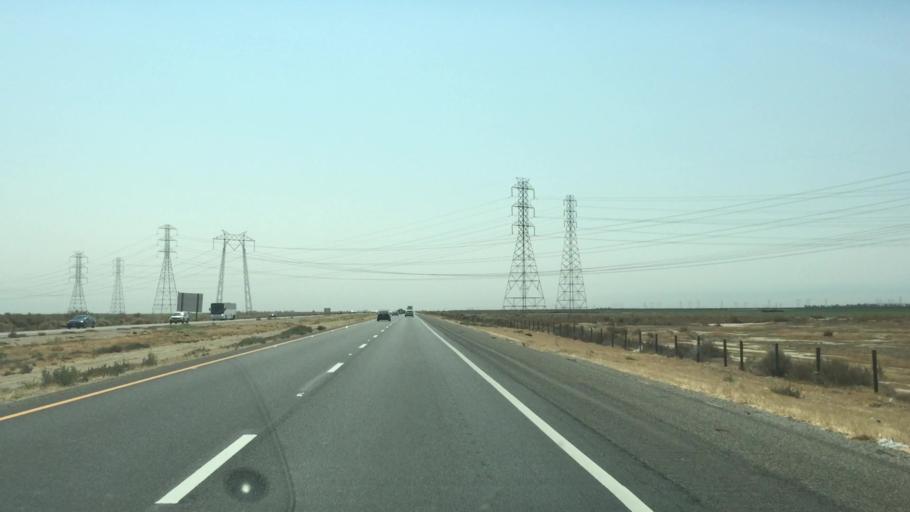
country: US
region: California
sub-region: Kern County
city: Buttonwillow
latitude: 35.3897
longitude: -119.3849
